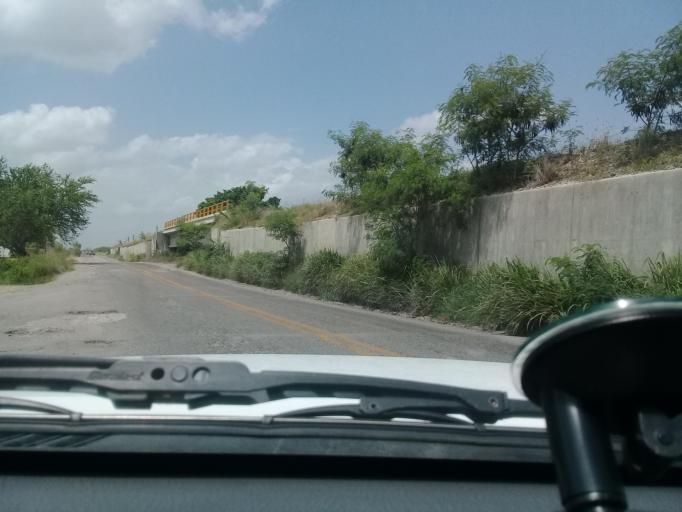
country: MX
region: Veracruz
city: Moralillo
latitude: 22.1833
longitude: -98.0188
